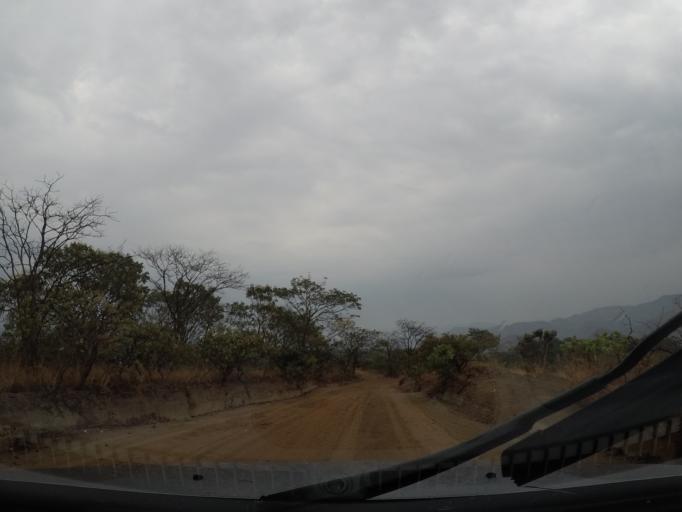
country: BR
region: Goias
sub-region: Pirenopolis
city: Pirenopolis
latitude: -15.8302
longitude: -48.9051
